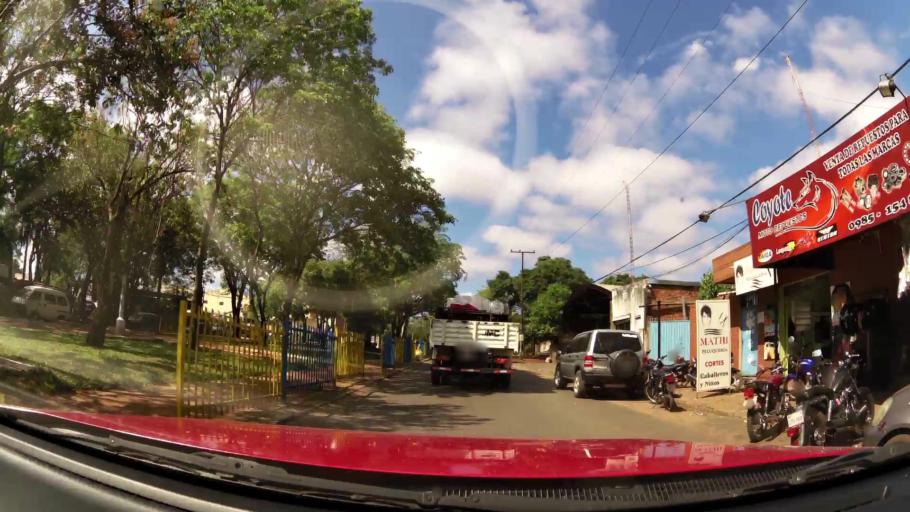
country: PY
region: Central
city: San Lorenzo
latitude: -25.2648
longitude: -57.4845
